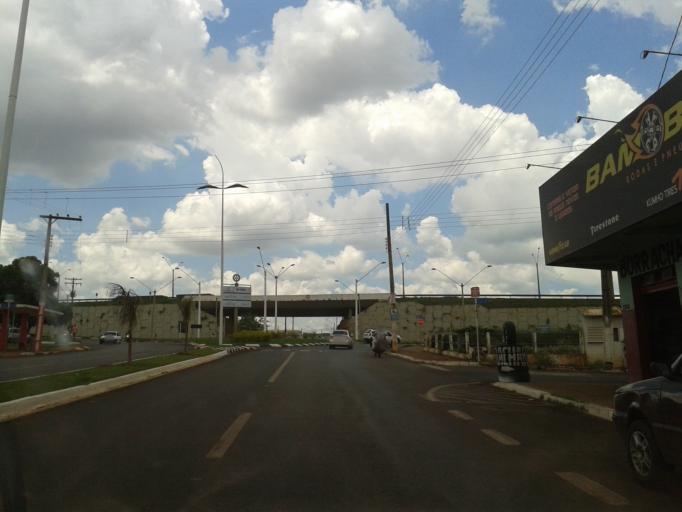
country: BR
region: Goias
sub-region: Itumbiara
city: Itumbiara
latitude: -18.4010
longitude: -49.2040
